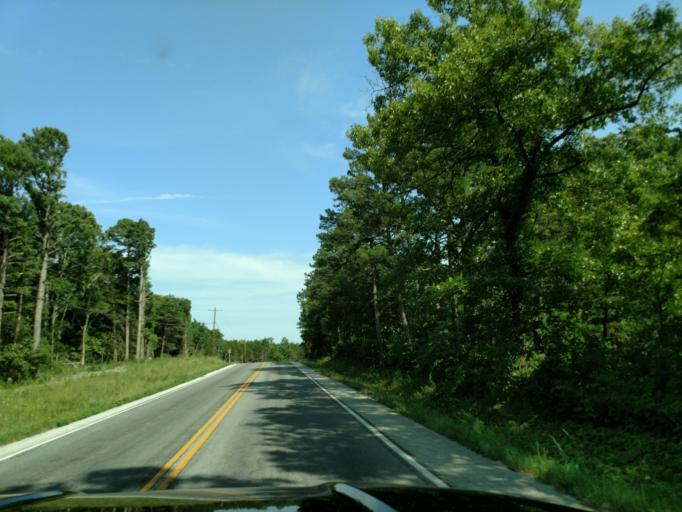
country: US
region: Missouri
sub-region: Barry County
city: Shell Knob
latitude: 36.6132
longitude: -93.5947
